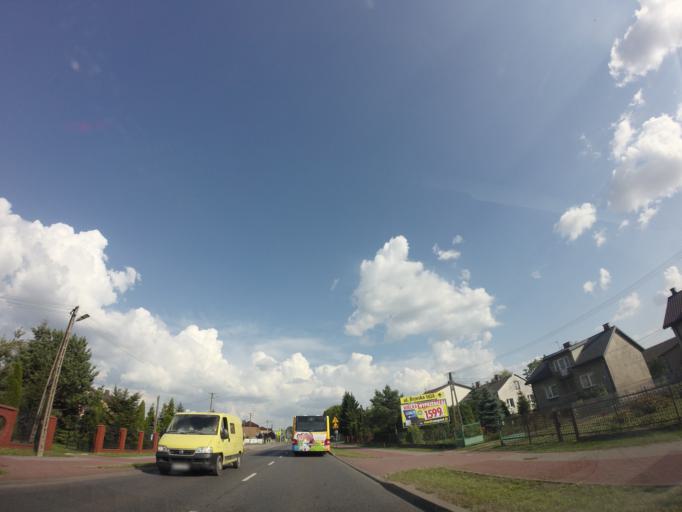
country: PL
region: Masovian Voivodeship
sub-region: Powiat siedlecki
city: Suchozebry
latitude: 52.2054
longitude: 22.2438
